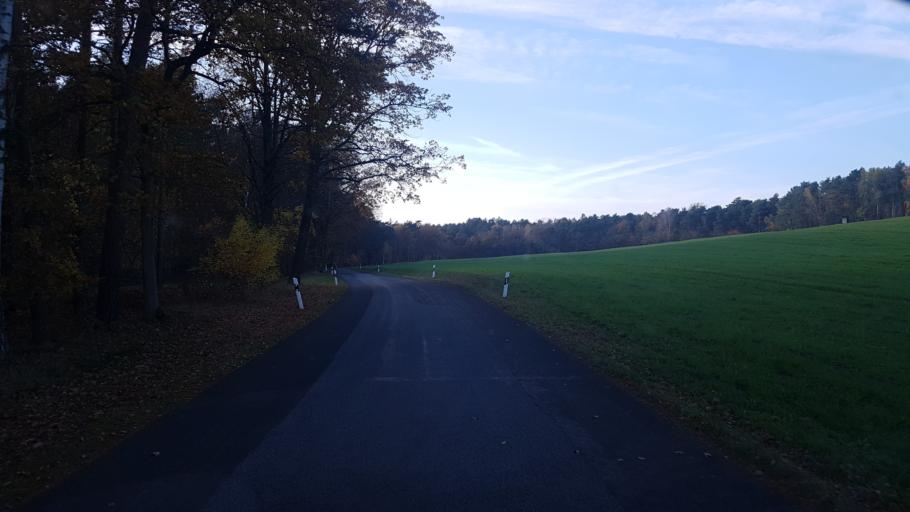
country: DE
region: Brandenburg
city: Altdobern
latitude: 51.6909
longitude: 13.9877
